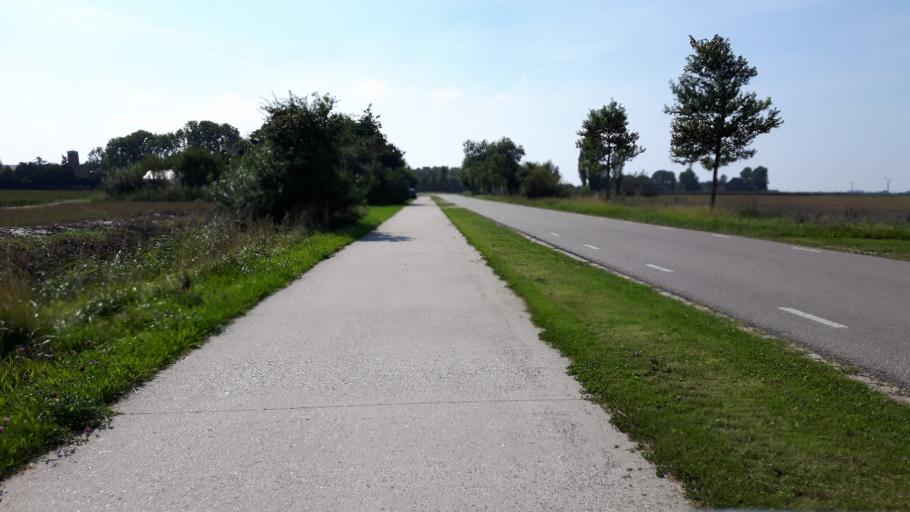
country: NL
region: Friesland
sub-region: Gemeente Franekeradeel
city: Tzummarum
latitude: 53.2123
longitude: 5.5608
